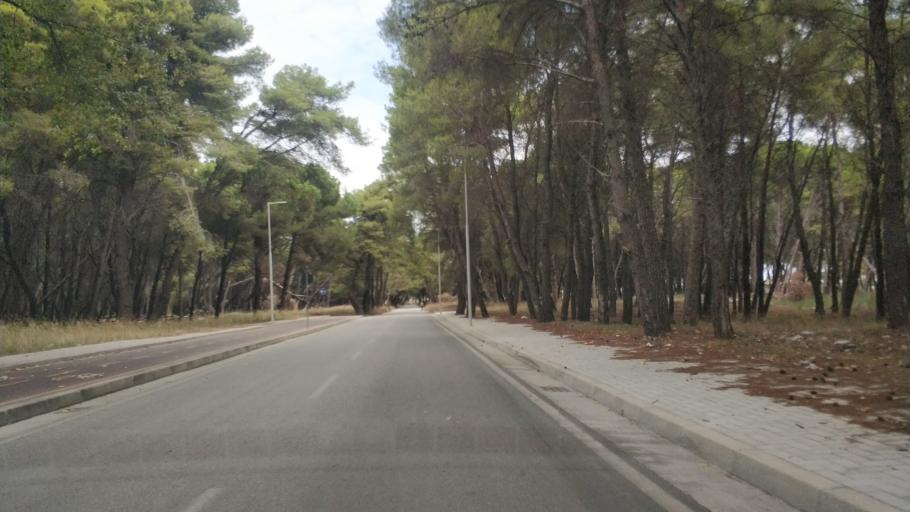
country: AL
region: Vlore
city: Vlore
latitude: 40.4668
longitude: 19.4616
